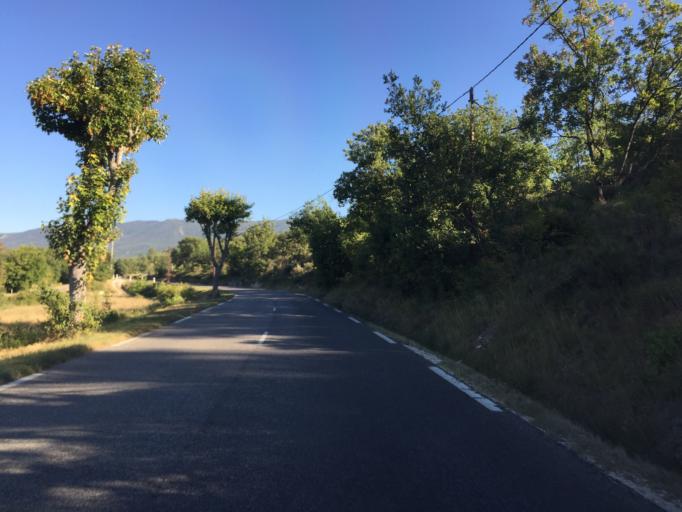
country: FR
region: Provence-Alpes-Cote d'Azur
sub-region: Departement du Vaucluse
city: Saignon
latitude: 43.8732
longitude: 5.4484
